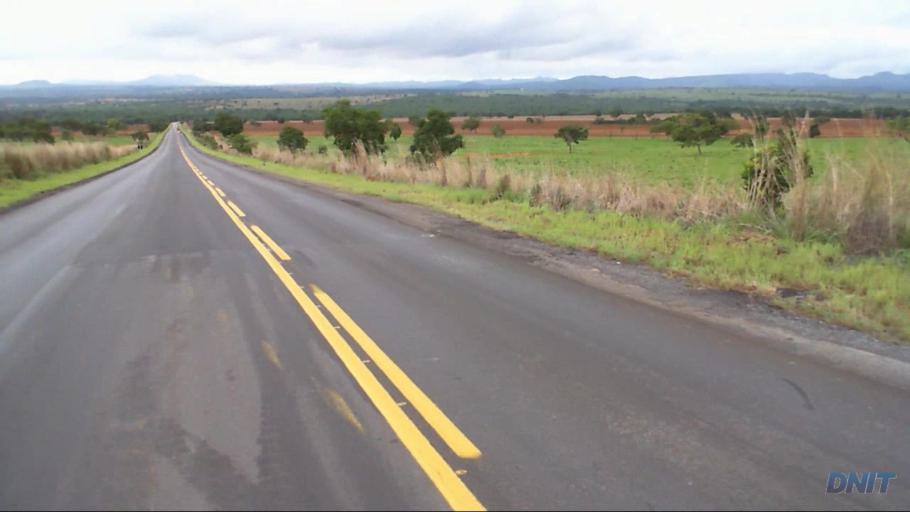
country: BR
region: Goias
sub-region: Padre Bernardo
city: Padre Bernardo
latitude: -15.2199
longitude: -48.5318
